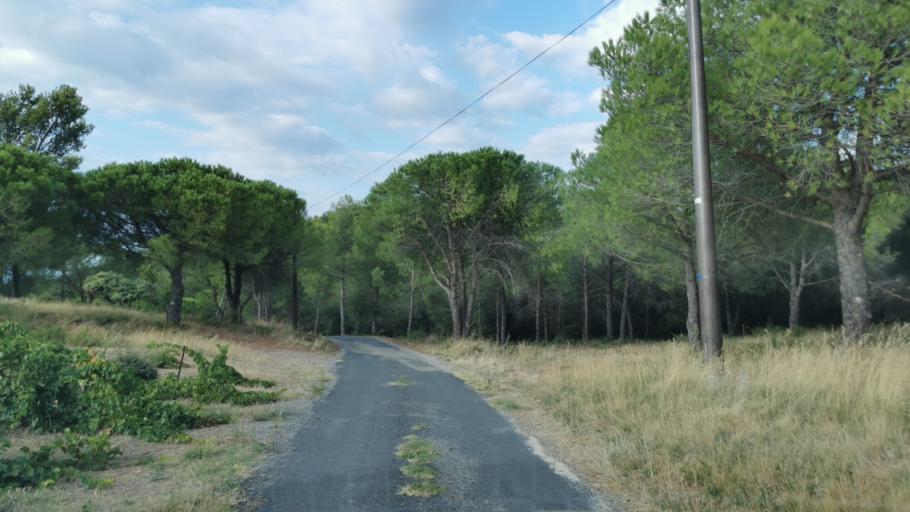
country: FR
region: Languedoc-Roussillon
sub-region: Departement de l'Aude
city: Bizanet
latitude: 43.1788
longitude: 2.8920
